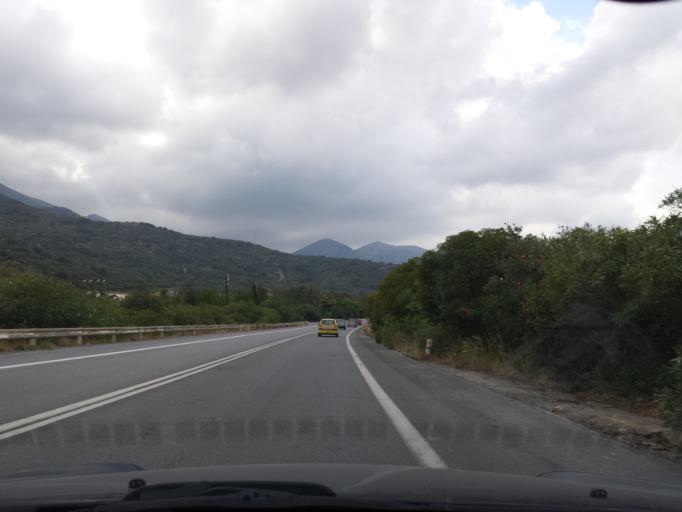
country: GR
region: Crete
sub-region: Nomos Lasithiou
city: Neapoli
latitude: 35.2606
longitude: 25.5994
